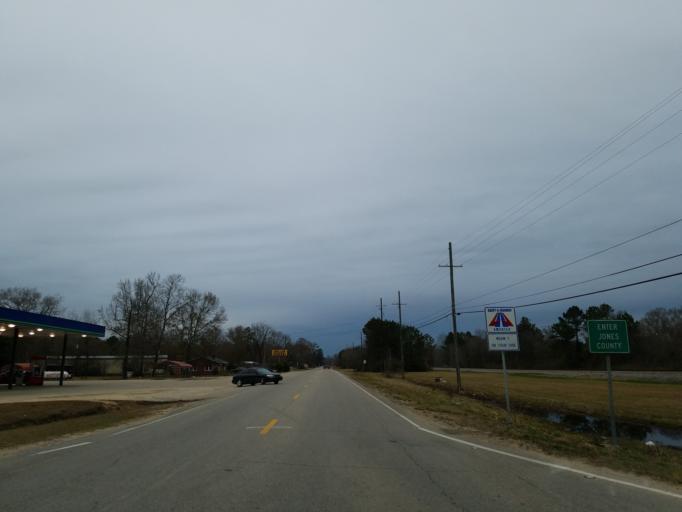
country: US
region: Mississippi
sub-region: Forrest County
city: Glendale
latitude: 31.4338
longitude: -89.2838
